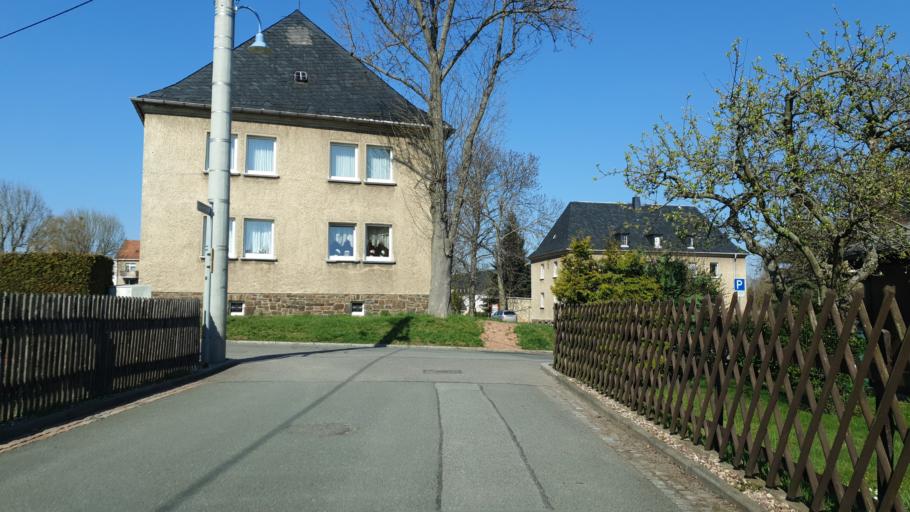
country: DE
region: Saxony
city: Oelsnitz
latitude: 50.7321
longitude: 12.7019
